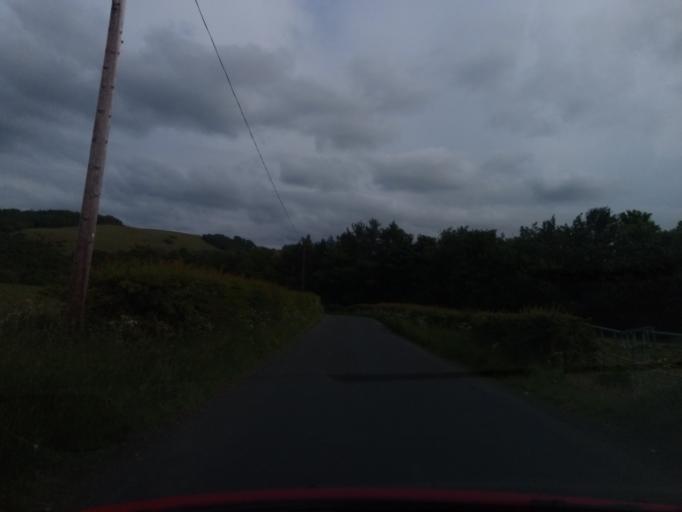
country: GB
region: Scotland
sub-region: The Scottish Borders
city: Galashiels
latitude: 55.5816
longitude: -2.8176
